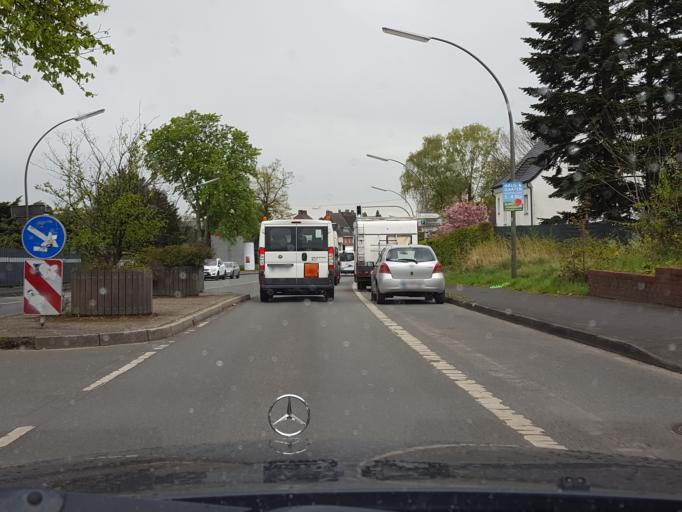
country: DE
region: North Rhine-Westphalia
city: Waltrop
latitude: 51.6224
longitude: 7.3916
